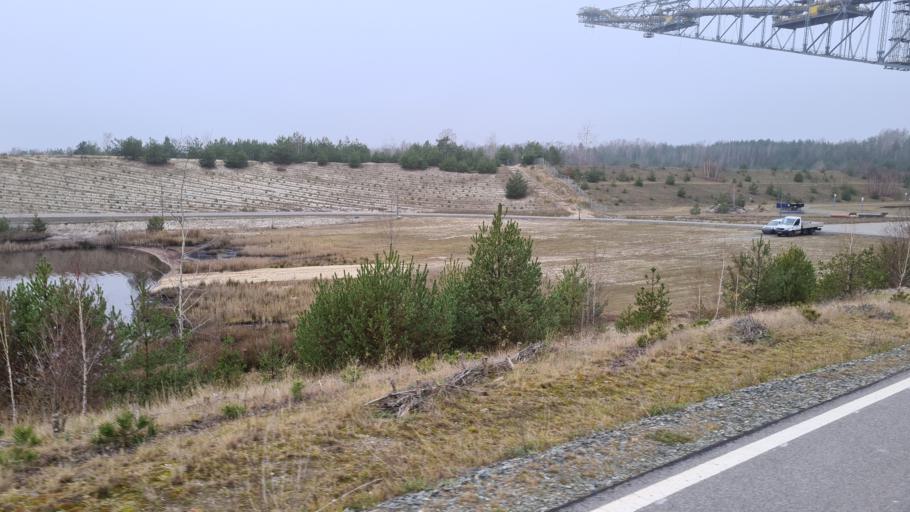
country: DE
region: Brandenburg
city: Sallgast
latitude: 51.5845
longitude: 13.7788
